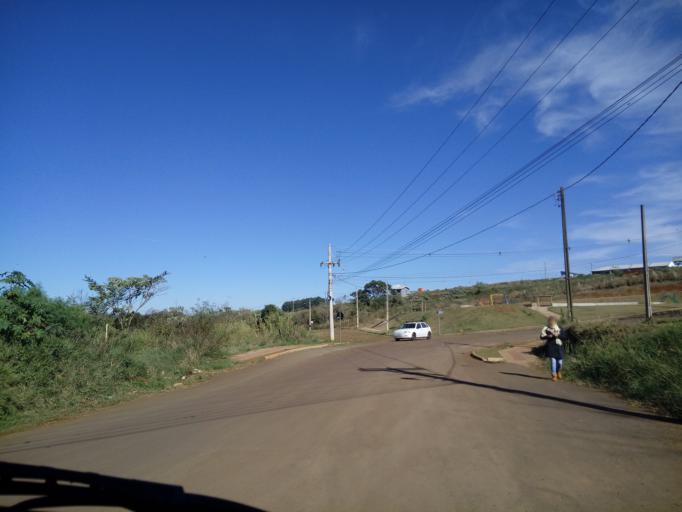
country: BR
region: Santa Catarina
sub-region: Chapeco
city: Chapeco
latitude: -27.0392
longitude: -52.6175
